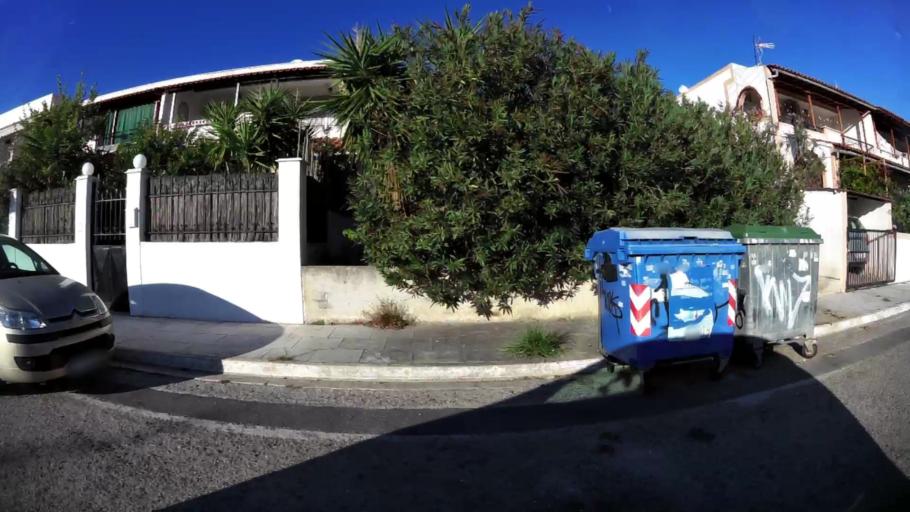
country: GR
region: Attica
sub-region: Nomarchia Anatolikis Attikis
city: Acharnes
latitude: 38.0869
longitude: 23.7197
